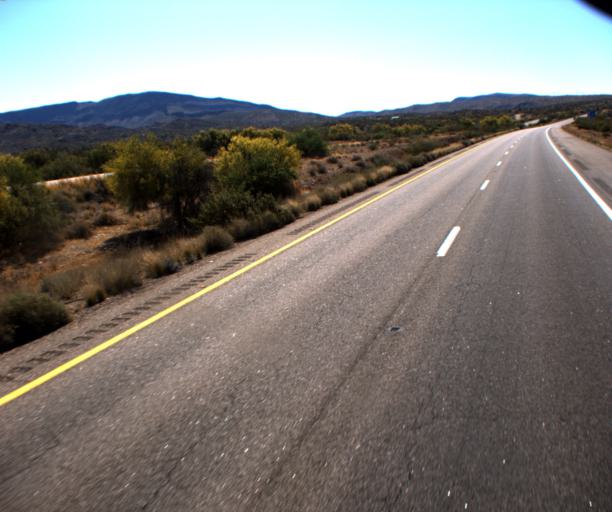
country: US
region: Arizona
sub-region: Yavapai County
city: Bagdad
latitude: 34.6285
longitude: -113.5408
